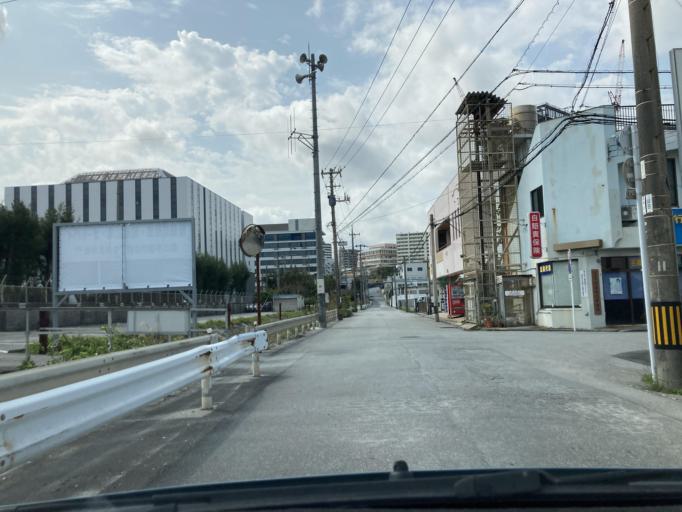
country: JP
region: Okinawa
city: Ginowan
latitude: 26.2724
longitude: 127.7152
